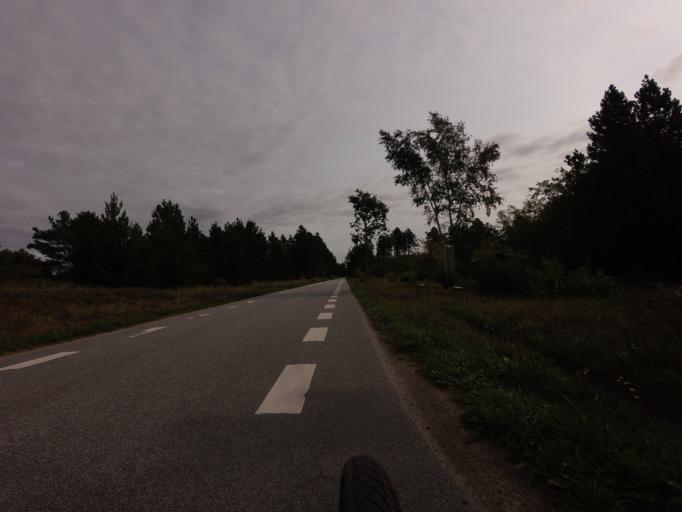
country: DK
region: North Denmark
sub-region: Hjorring Kommune
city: Sindal
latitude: 57.5893
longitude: 10.2224
